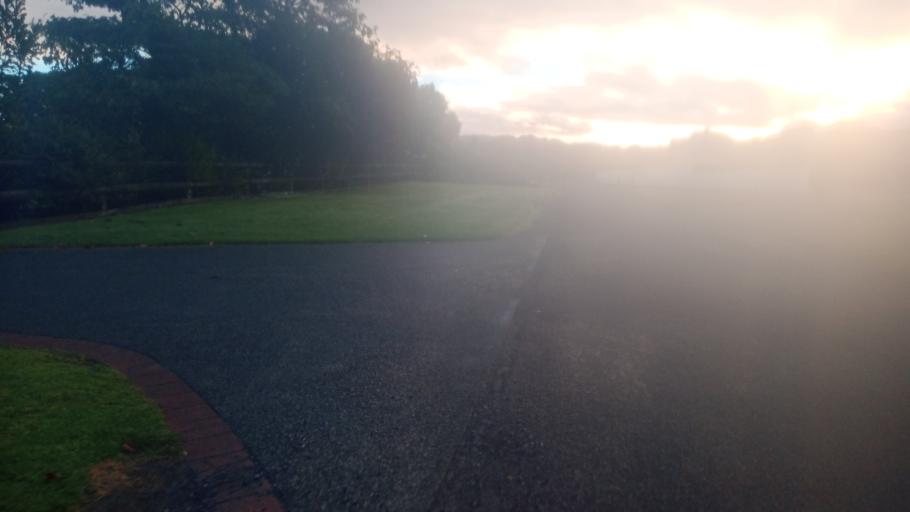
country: NZ
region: Gisborne
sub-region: Gisborne District
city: Gisborne
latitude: -38.6407
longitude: 177.9889
